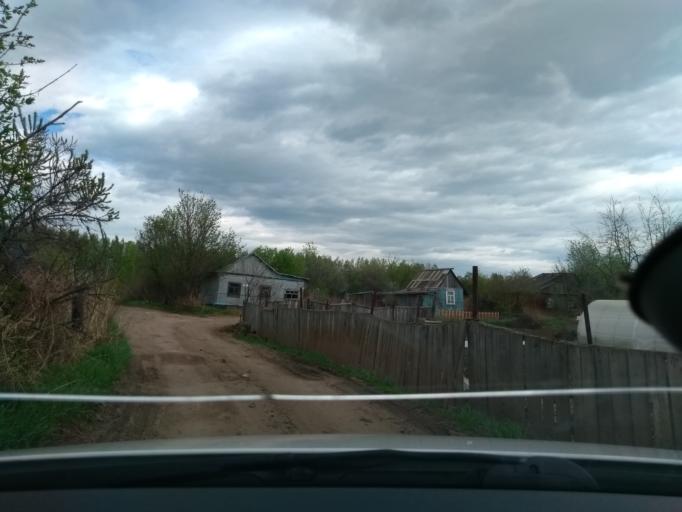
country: RU
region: Perm
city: Lobanovo
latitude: 57.8682
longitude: 56.3048
